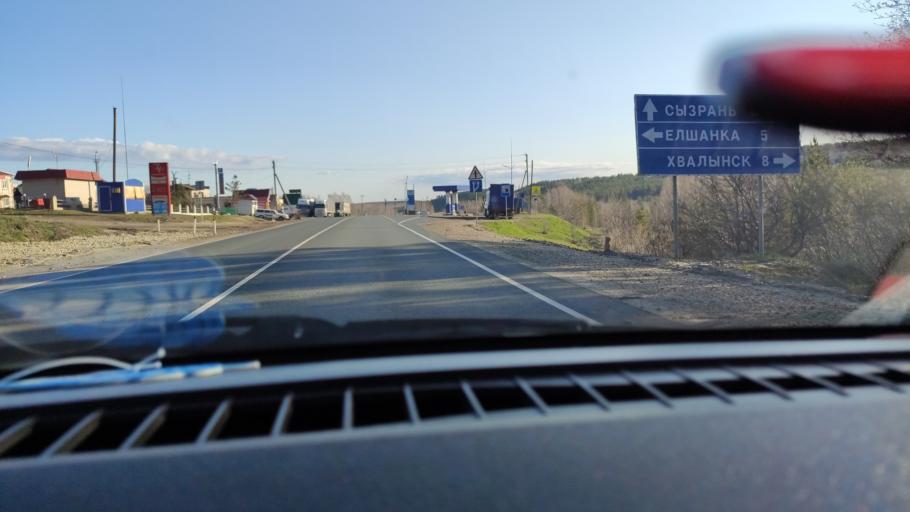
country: RU
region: Saratov
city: Khvalynsk
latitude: 52.5231
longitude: 48.0208
